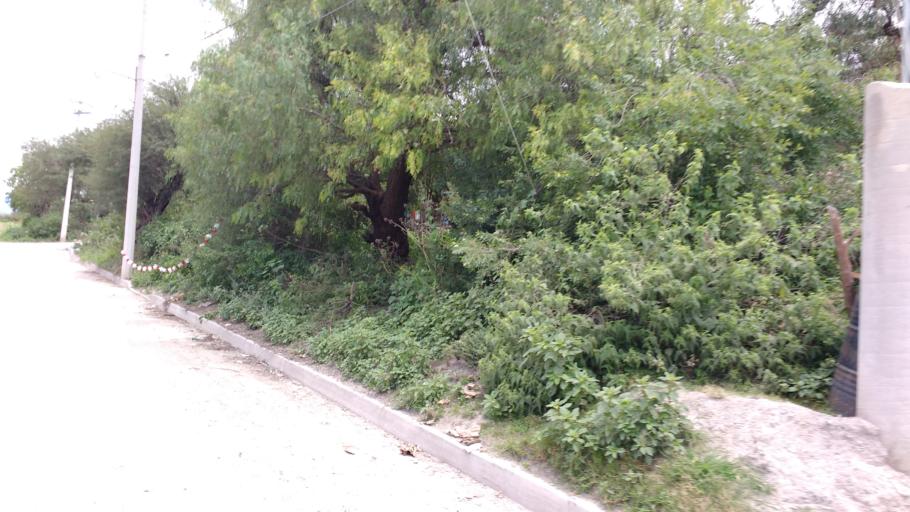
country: MX
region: Hidalgo
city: Mixquiahuala de Juarez
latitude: 20.2527
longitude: -99.2418
